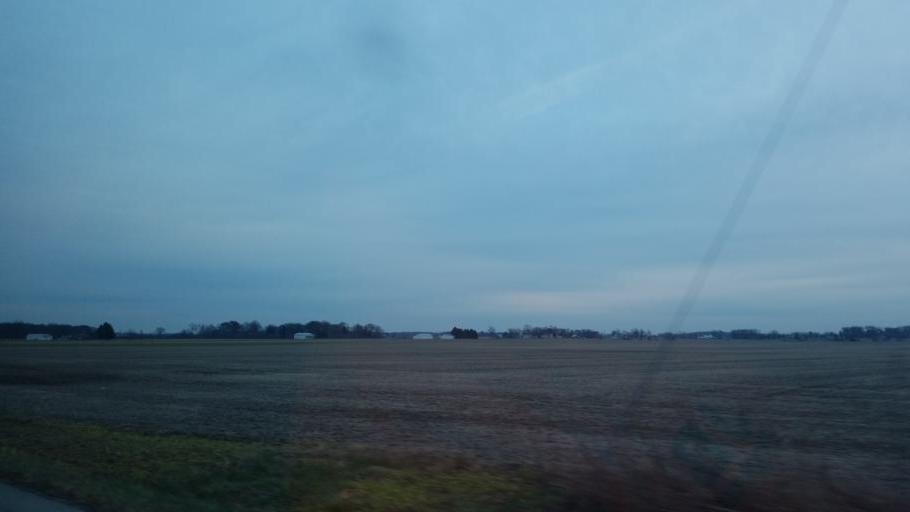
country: US
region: Indiana
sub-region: Adams County
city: Decatur
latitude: 40.7890
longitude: -84.9069
